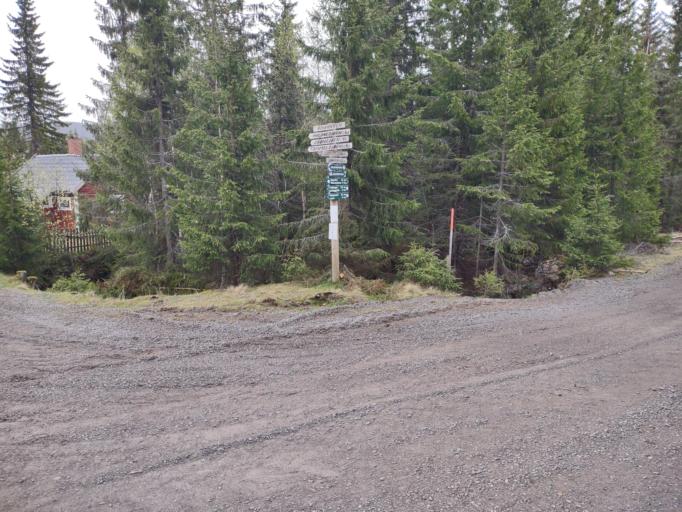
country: NO
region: Oppland
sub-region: Gran
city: Jaren
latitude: 60.4136
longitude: 10.7191
